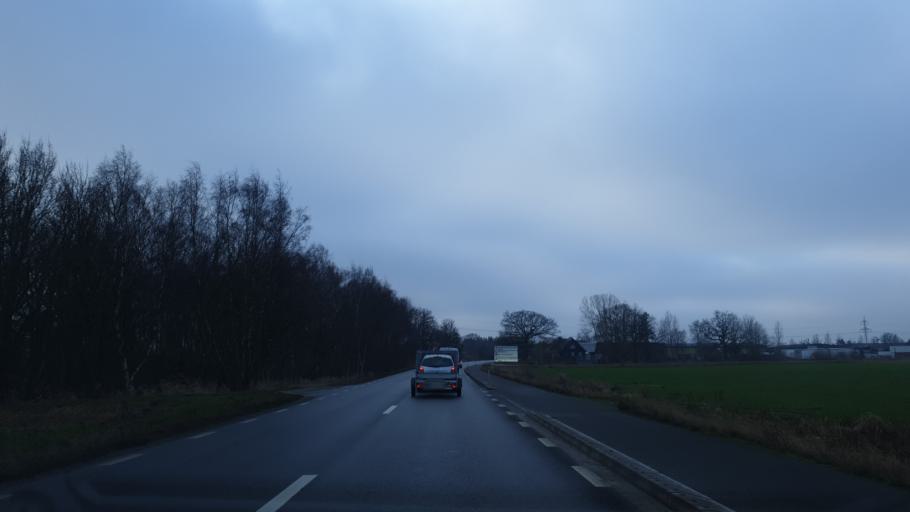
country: SE
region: Blekinge
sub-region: Solvesborgs Kommun
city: Soelvesborg
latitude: 56.0681
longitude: 14.6331
